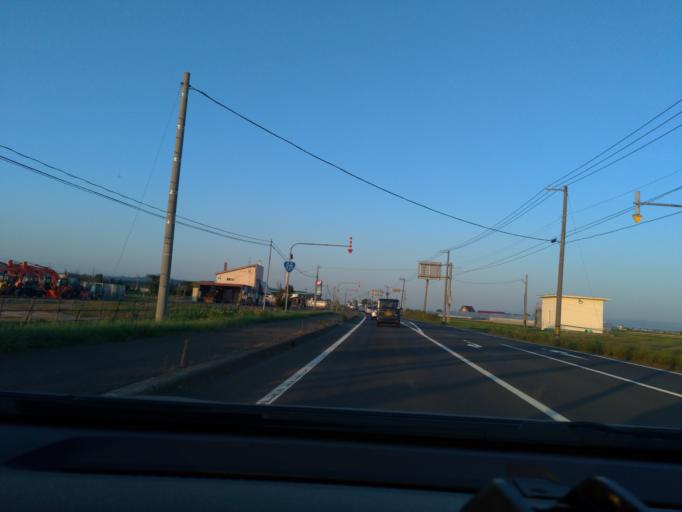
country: JP
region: Hokkaido
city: Tobetsu
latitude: 43.2158
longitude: 141.5304
